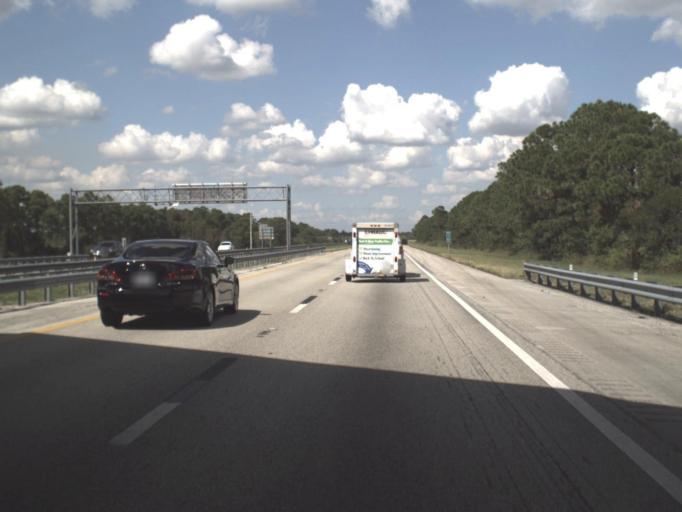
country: US
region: Florida
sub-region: Saint Lucie County
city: Lakewood Park
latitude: 27.4330
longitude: -80.4183
